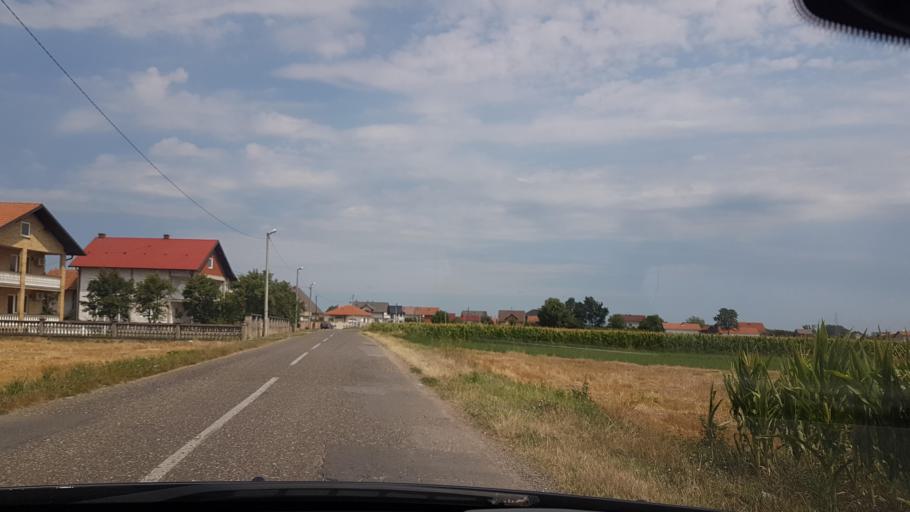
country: BA
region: Republika Srpska
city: Bijeljina
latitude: 44.7999
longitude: 19.2172
